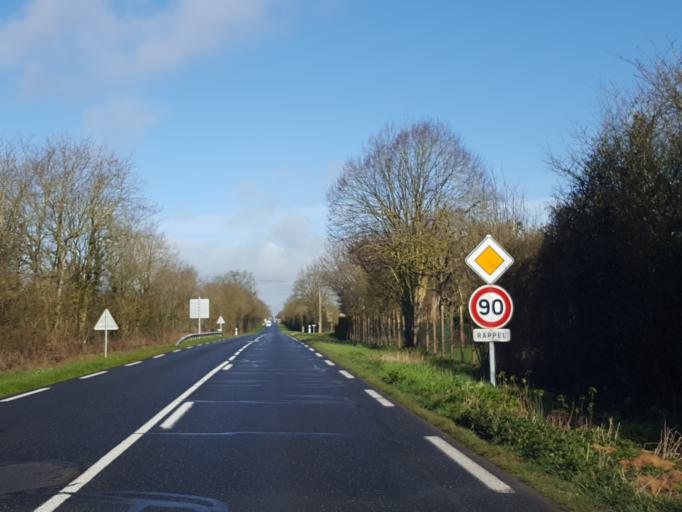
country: FR
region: Pays de la Loire
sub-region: Departement de la Vendee
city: Saligny
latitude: 46.7976
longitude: -1.4457
